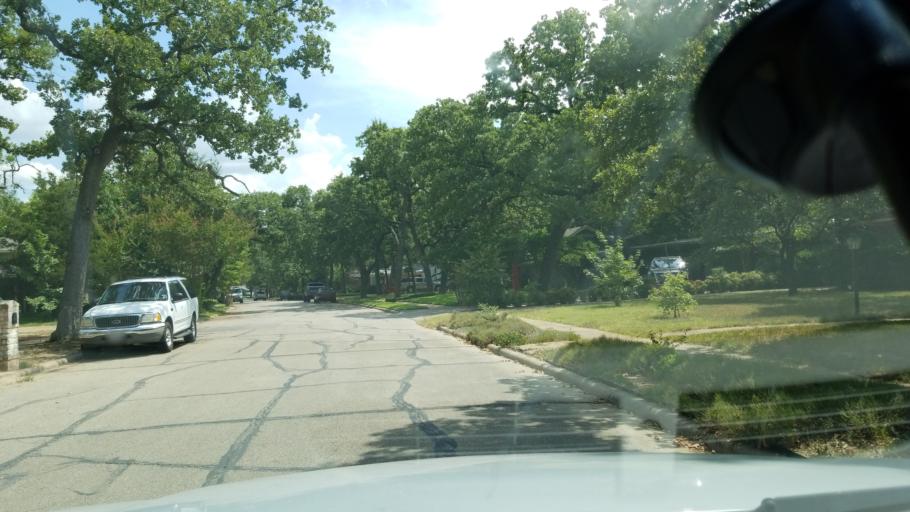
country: US
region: Texas
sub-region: Dallas County
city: Irving
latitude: 32.8210
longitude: -96.9841
